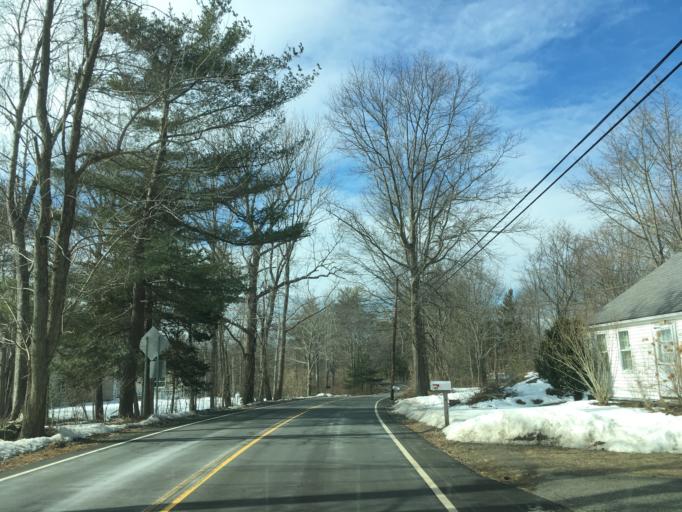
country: US
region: New Hampshire
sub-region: Rockingham County
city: North Hampton
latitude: 42.9898
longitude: -70.8775
